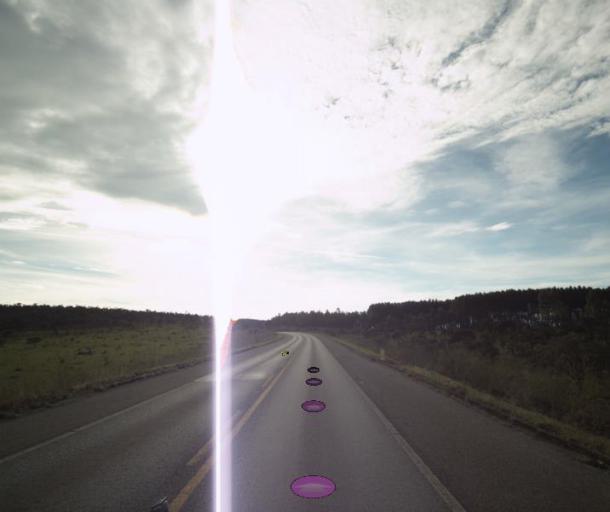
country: BR
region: Goias
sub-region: Pirenopolis
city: Pirenopolis
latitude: -15.7505
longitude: -48.6079
